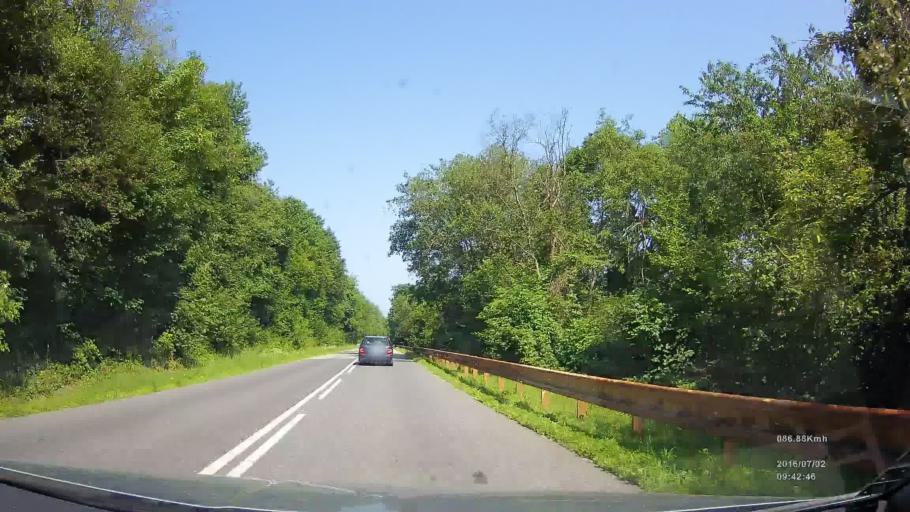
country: SK
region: Kosicky
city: Gelnica
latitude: 48.8456
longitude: 21.0360
